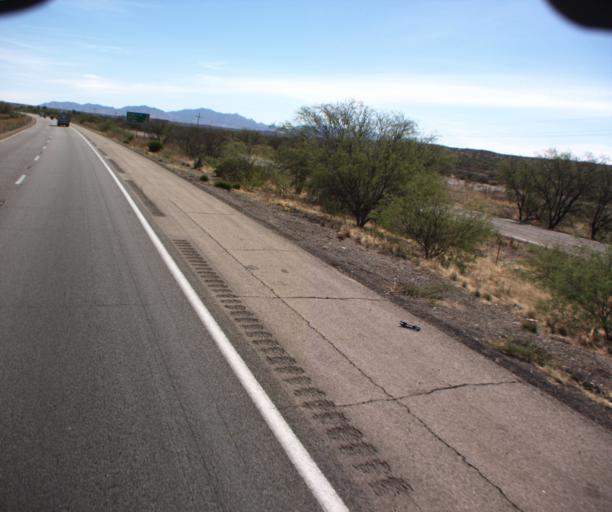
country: US
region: Arizona
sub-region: Cochise County
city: Benson
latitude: 31.9654
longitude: -110.2554
